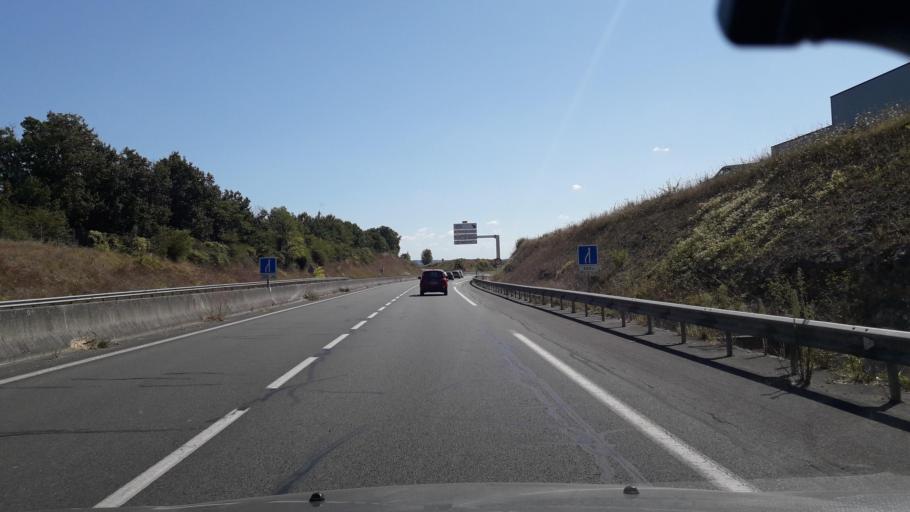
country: FR
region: Poitou-Charentes
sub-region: Departement de la Charente
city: Saint-Yrieix-sur-Charente
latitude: 45.6803
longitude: 0.1272
